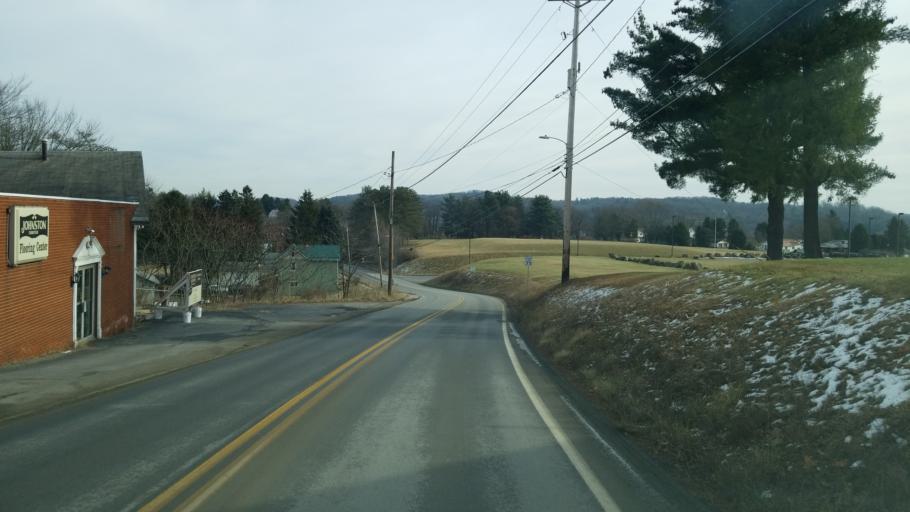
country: US
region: Pennsylvania
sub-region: Jefferson County
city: Punxsutawney
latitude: 40.9495
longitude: -78.9783
